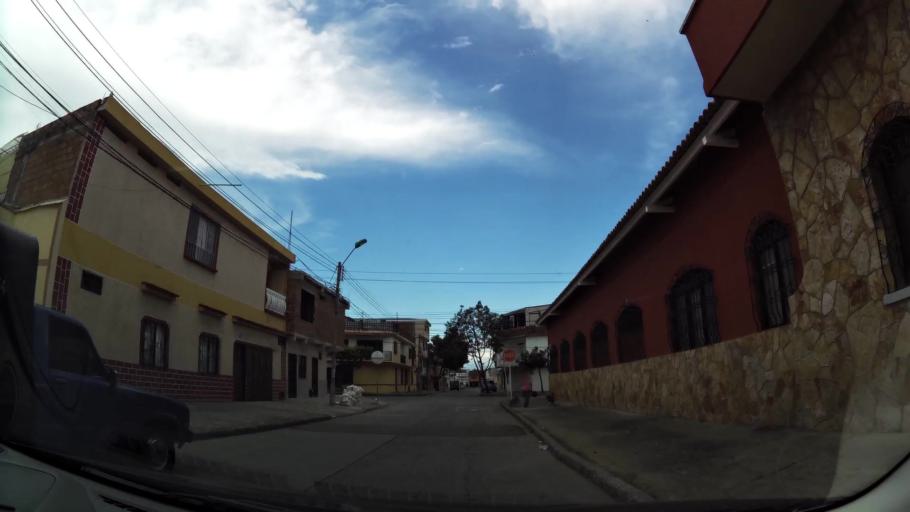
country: CO
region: Valle del Cauca
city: Cali
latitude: 3.4398
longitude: -76.5217
